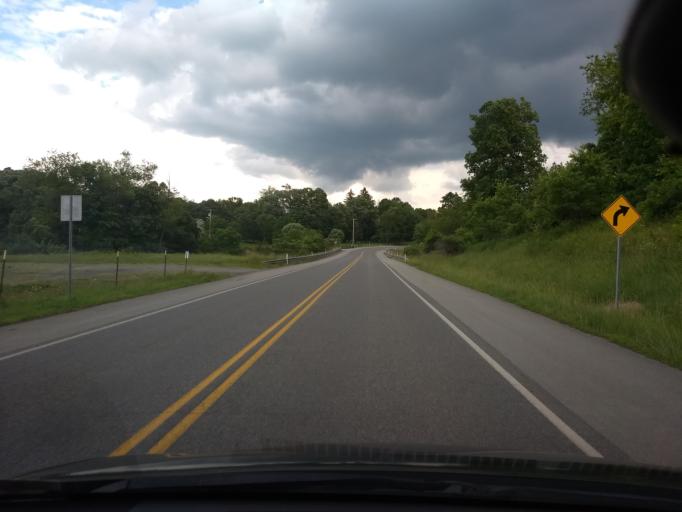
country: US
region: Pennsylvania
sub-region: Westmoreland County
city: Avonmore
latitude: 40.5195
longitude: -79.4854
